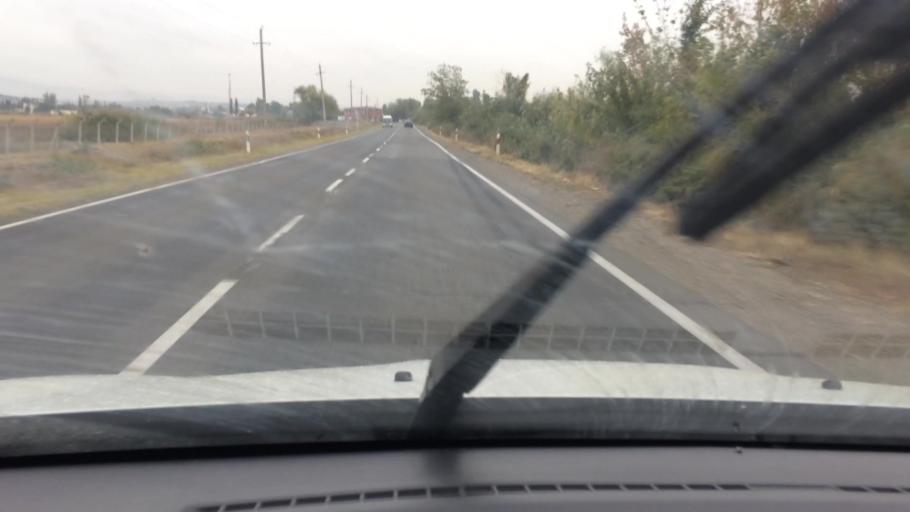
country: GE
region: Kvemo Kartli
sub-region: Marneuli
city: Marneuli
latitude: 41.4672
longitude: 44.8044
